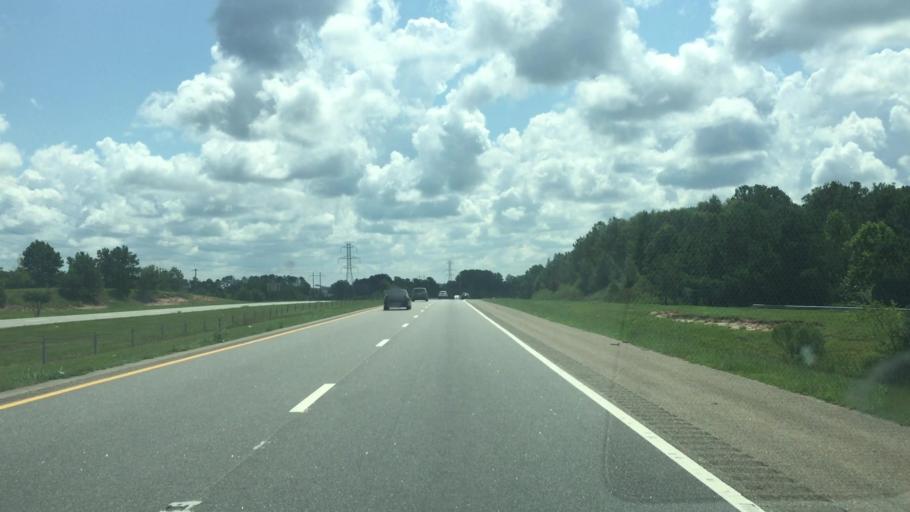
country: US
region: North Carolina
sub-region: Richmond County
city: Cordova
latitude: 34.9311
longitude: -79.8296
